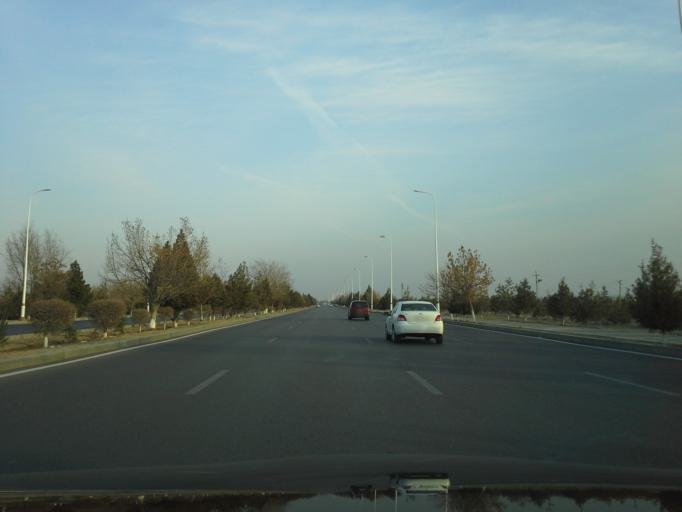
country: TM
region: Ahal
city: Abadan
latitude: 38.0398
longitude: 58.2123
